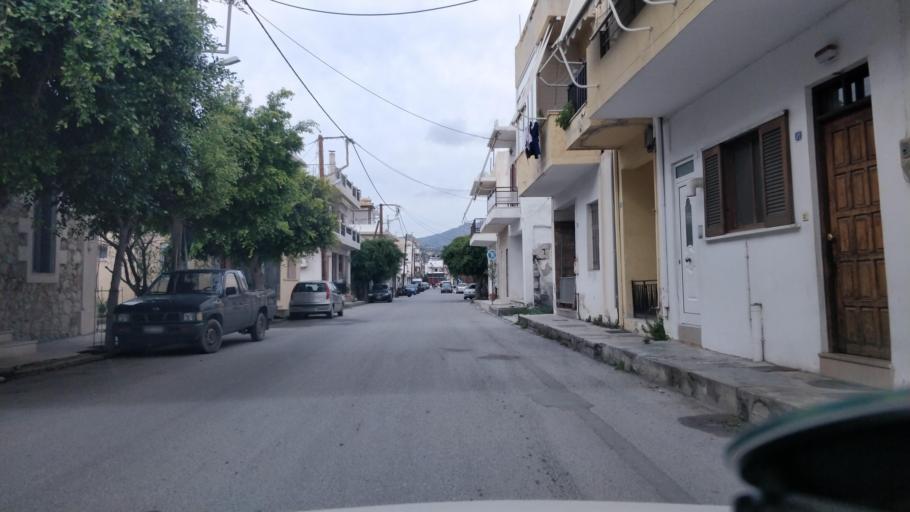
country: GR
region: Crete
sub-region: Nomos Lasithiou
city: Ierapetra
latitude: 35.0058
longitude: 25.7352
